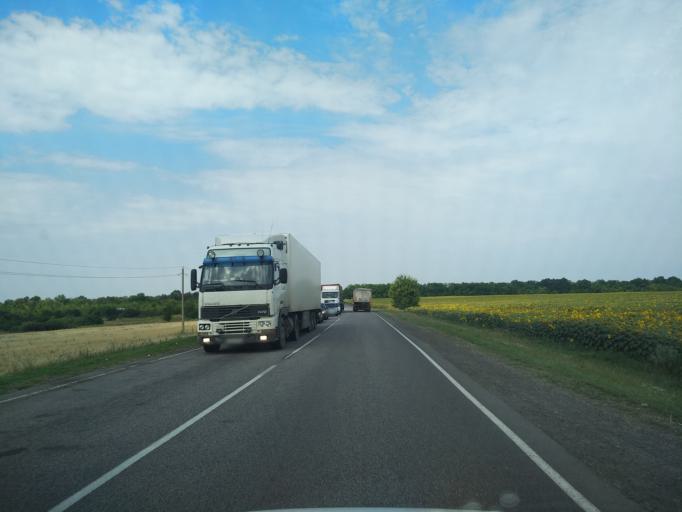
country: RU
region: Voronezj
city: Verkhnyaya Khava
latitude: 51.6781
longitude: 39.7983
